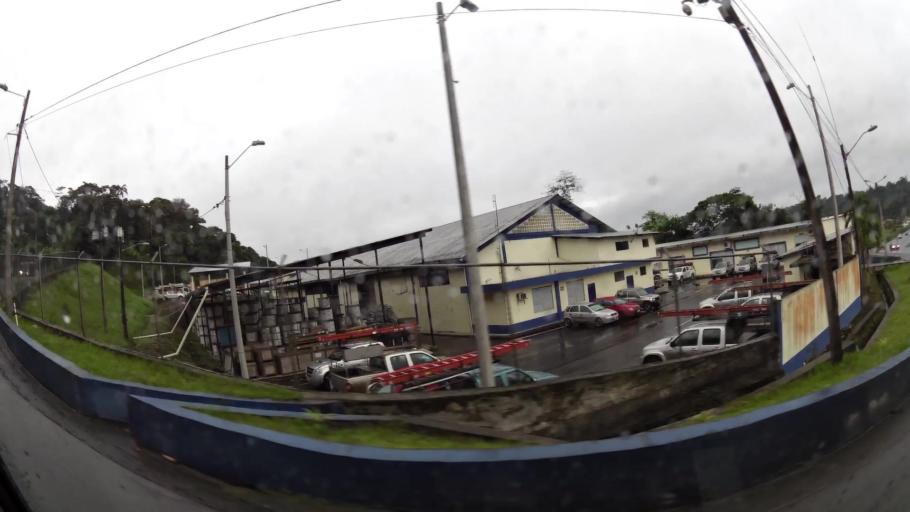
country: EC
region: Santo Domingo de los Tsachilas
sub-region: Canton Santo Domingo de los Colorados
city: Santo Domingo de los Colorados
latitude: -0.2493
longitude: -79.1395
